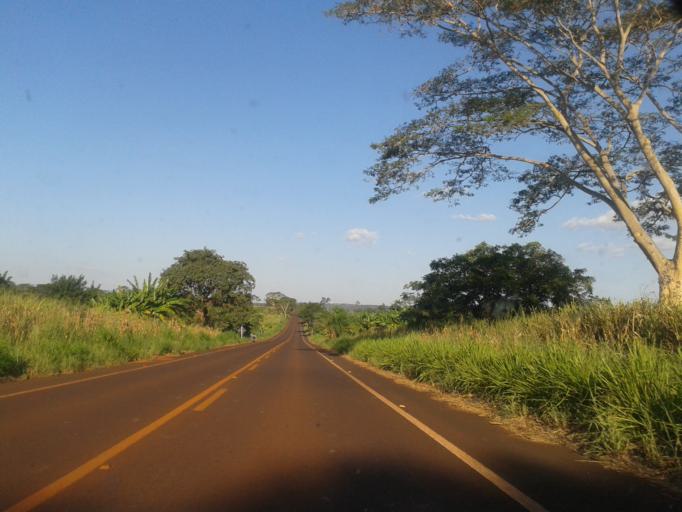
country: BR
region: Minas Gerais
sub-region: Santa Vitoria
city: Santa Vitoria
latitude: -18.7050
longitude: -49.8657
